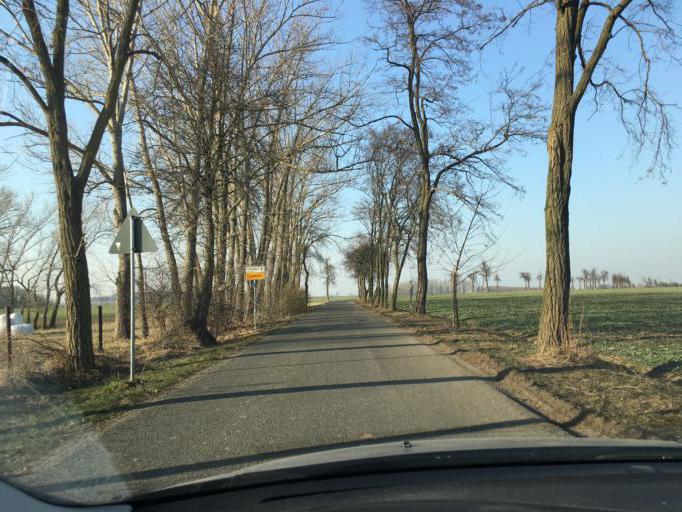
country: DE
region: Saxony
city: Kitzscher
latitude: 51.1583
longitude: 12.5906
